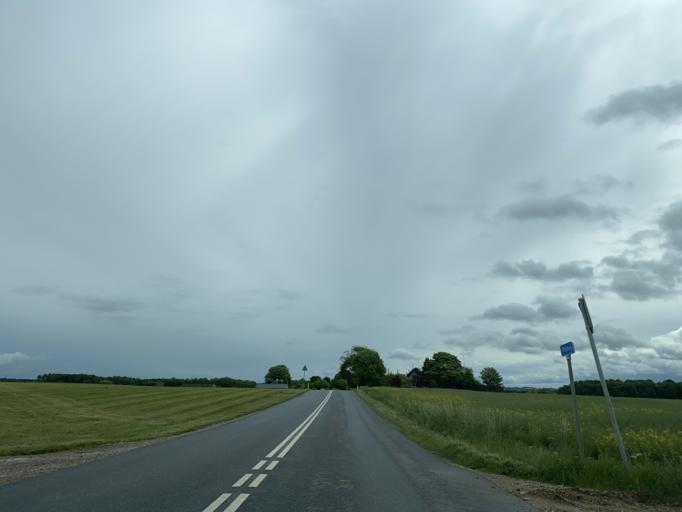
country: DK
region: Central Jutland
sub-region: Arhus Kommune
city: Sabro
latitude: 56.2498
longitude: 9.9965
